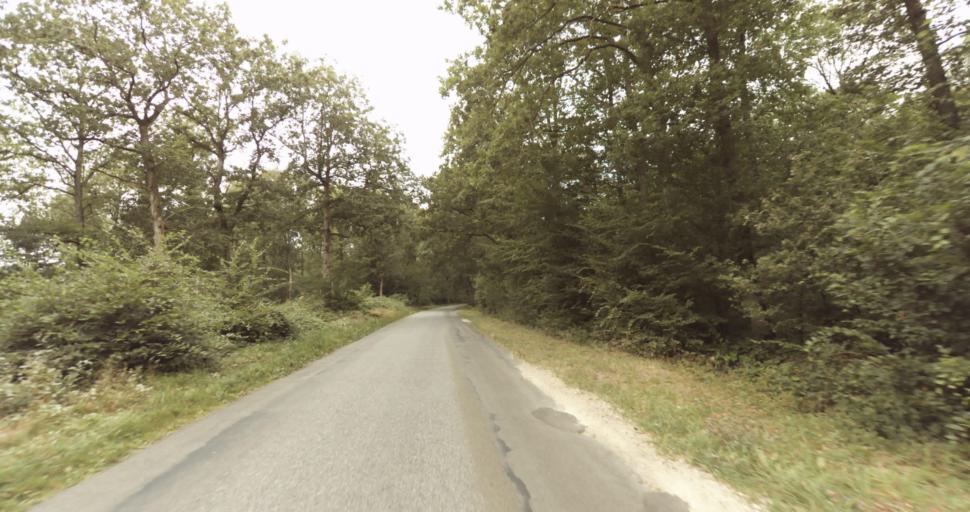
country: FR
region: Centre
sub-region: Departement d'Eure-et-Loir
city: Saint-Lubin-des-Joncherets
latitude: 48.7499
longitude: 1.2236
